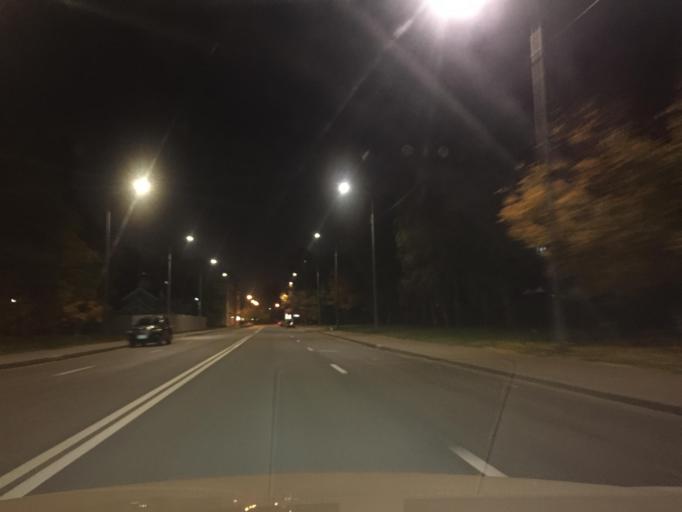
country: RU
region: Leningrad
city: Krestovskiy ostrov
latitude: 59.9724
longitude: 30.2710
